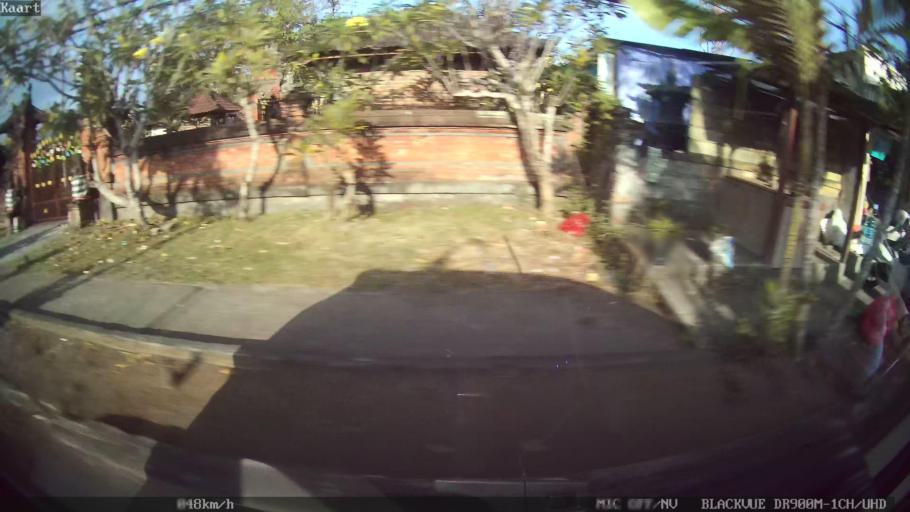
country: ID
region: Bali
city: Banjar Batur
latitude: -8.5931
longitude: 115.2153
